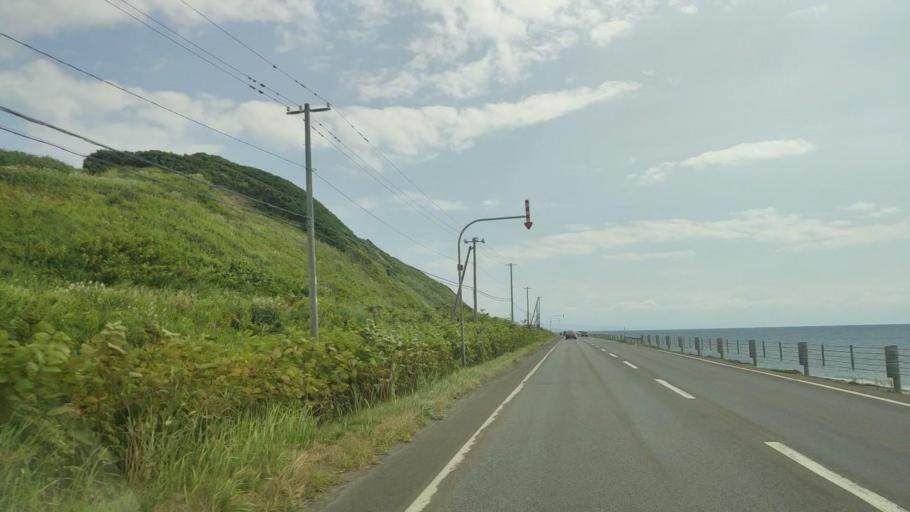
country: JP
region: Hokkaido
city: Rumoi
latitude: 44.1002
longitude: 141.6605
